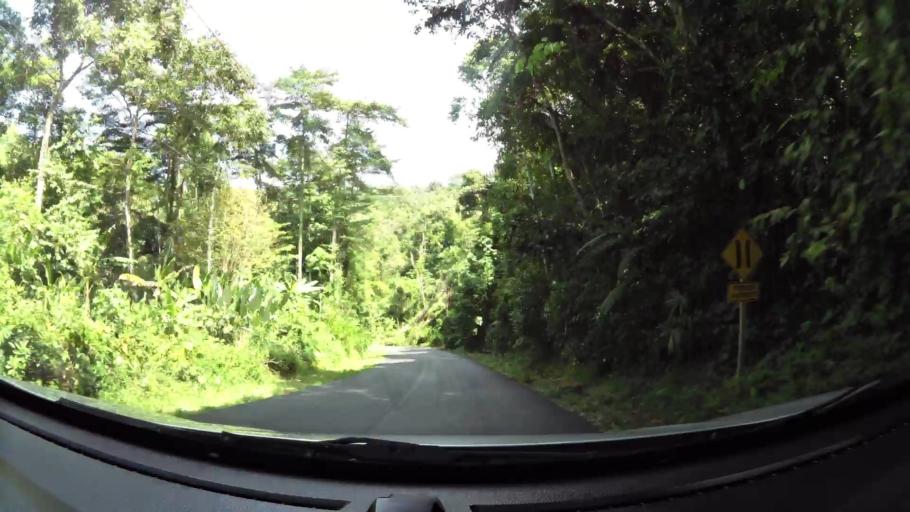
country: CR
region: San Jose
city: San Isidro
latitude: 9.2808
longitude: -83.8231
